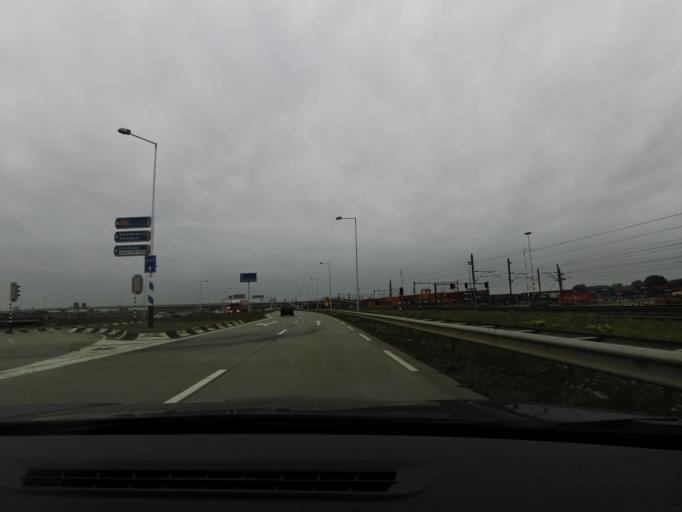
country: NL
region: South Holland
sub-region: Gemeente Albrandswaard
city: Rhoon
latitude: 51.8779
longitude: 4.3948
